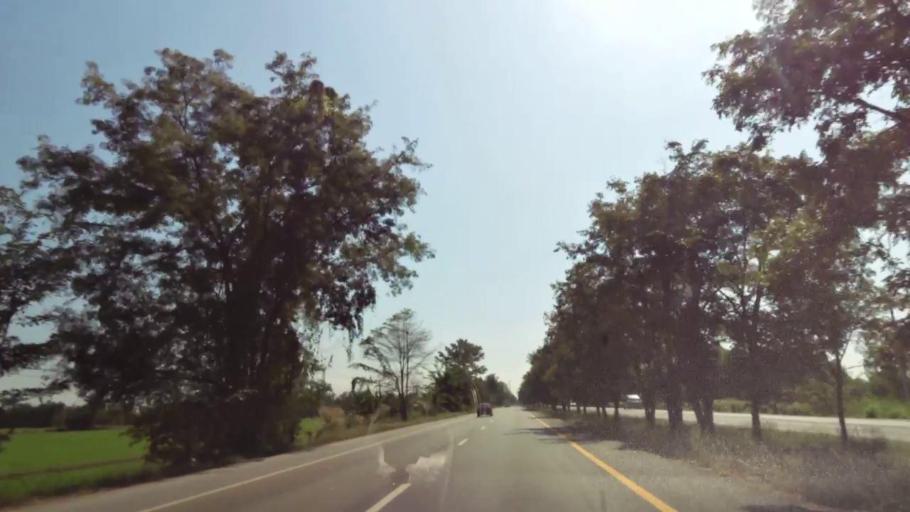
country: TH
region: Nakhon Sawan
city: Kao Liao
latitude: 15.8839
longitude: 100.1153
